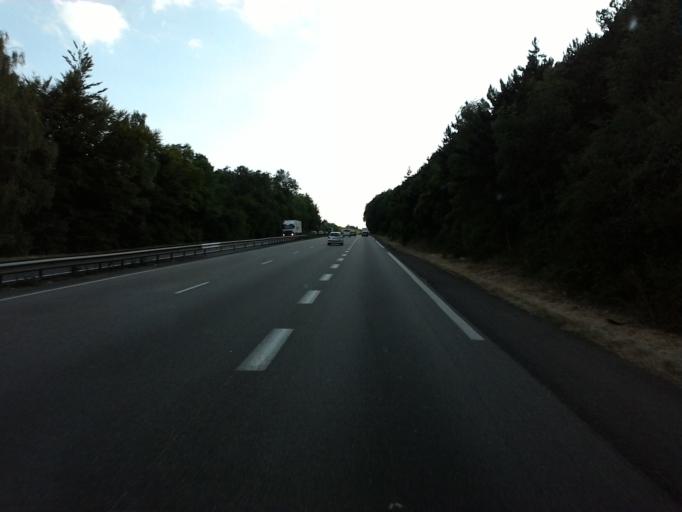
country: FR
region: Lorraine
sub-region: Departement de Meurthe-et-Moselle
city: Maxeville
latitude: 48.7107
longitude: 6.1457
